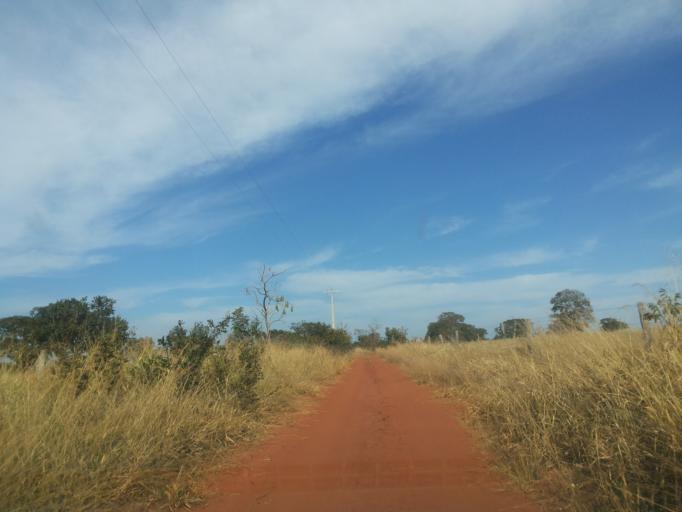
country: BR
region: Minas Gerais
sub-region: Ituiutaba
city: Ituiutaba
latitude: -19.1220
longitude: -49.3861
